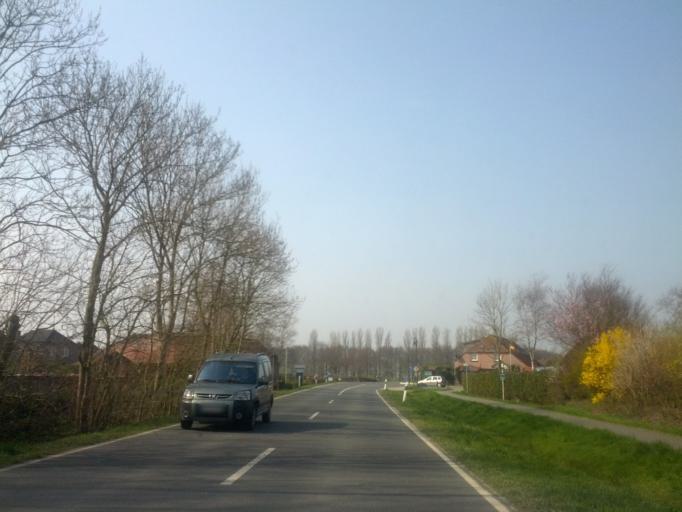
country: DE
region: Lower Saxony
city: Dornum
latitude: 53.6723
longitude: 7.4416
